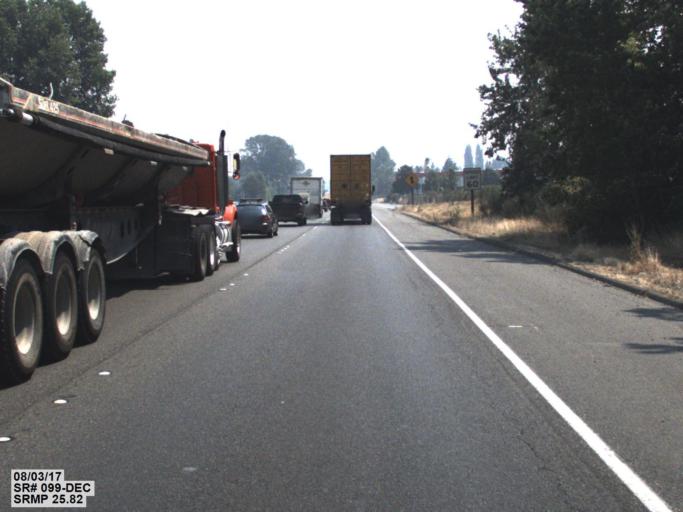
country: US
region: Washington
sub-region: King County
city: White Center
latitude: 47.5315
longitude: -122.3297
